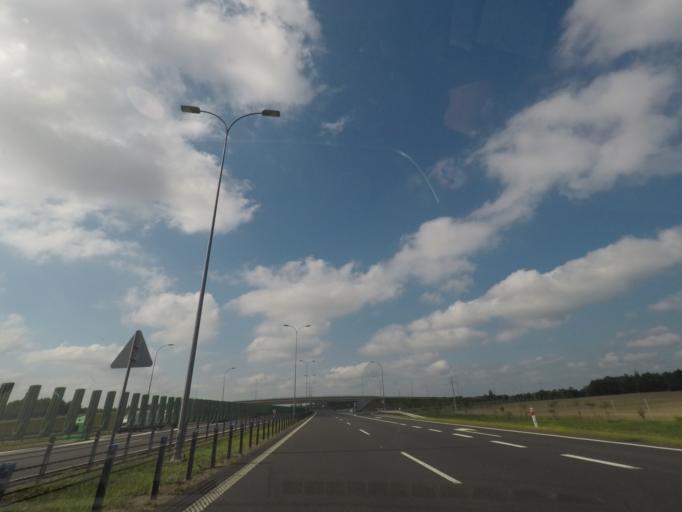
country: PL
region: Kujawsko-Pomorskie
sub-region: Powiat swiecki
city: Warlubie
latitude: 53.6065
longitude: 18.6239
